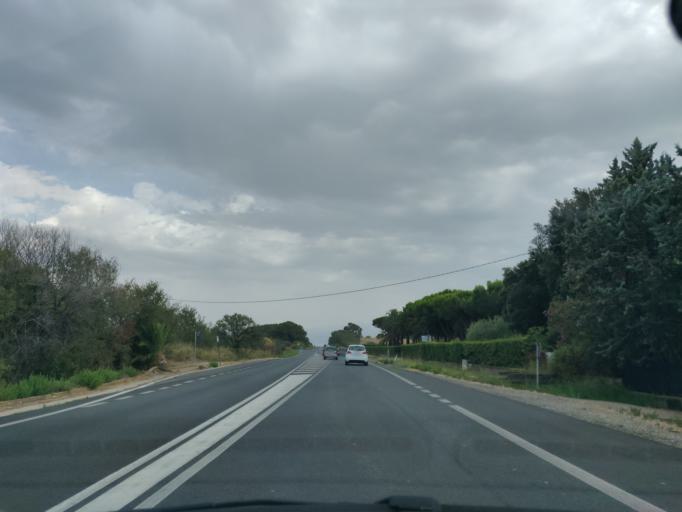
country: IT
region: Latium
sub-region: Citta metropolitana di Roma Capitale
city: Santa Marinella
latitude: 42.0326
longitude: 11.9328
